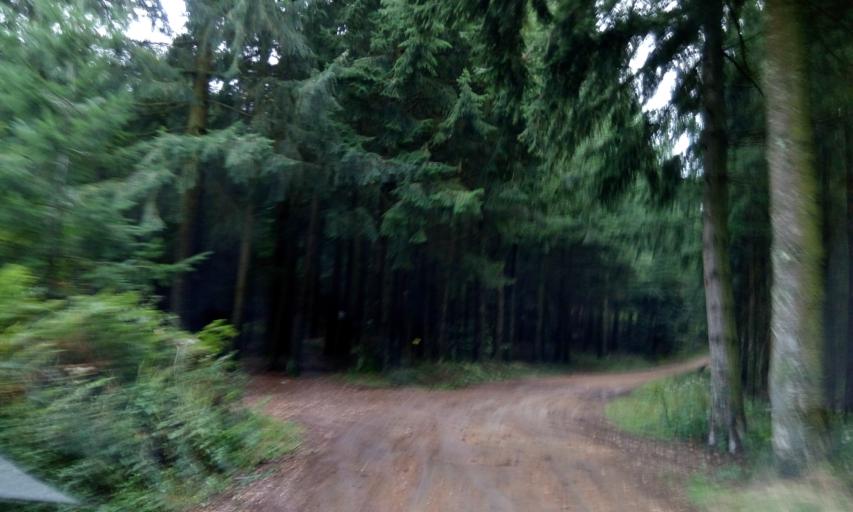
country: FR
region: Rhone-Alpes
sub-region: Departement du Rhone
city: Cublize
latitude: 46.0233
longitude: 4.4276
